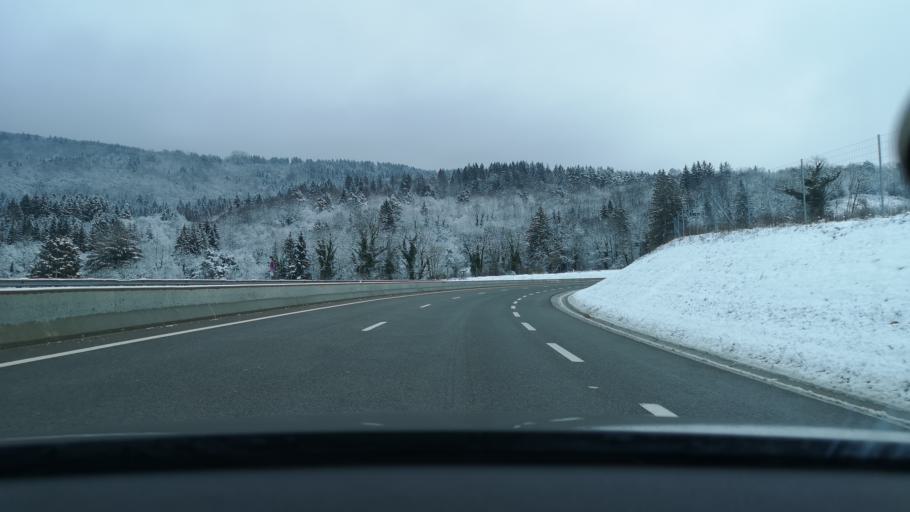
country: FR
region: Rhone-Alpes
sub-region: Departement de l'Ain
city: Dortan
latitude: 46.3233
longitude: 5.6730
